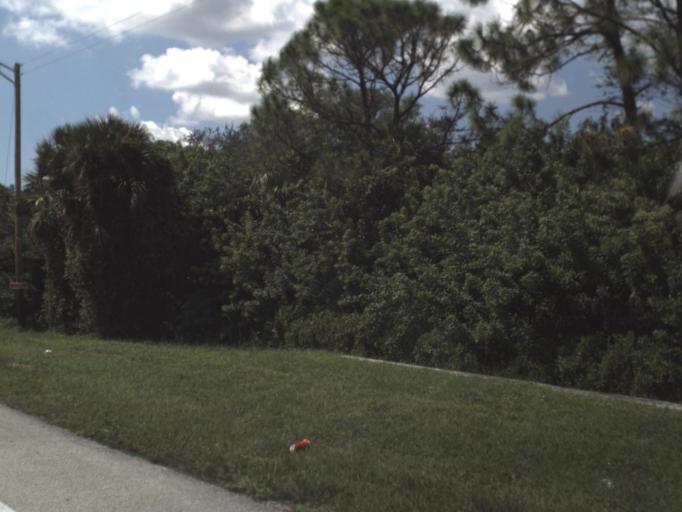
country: US
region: Florida
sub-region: Lee County
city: Fort Myers Shores
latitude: 26.7189
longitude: -81.7651
